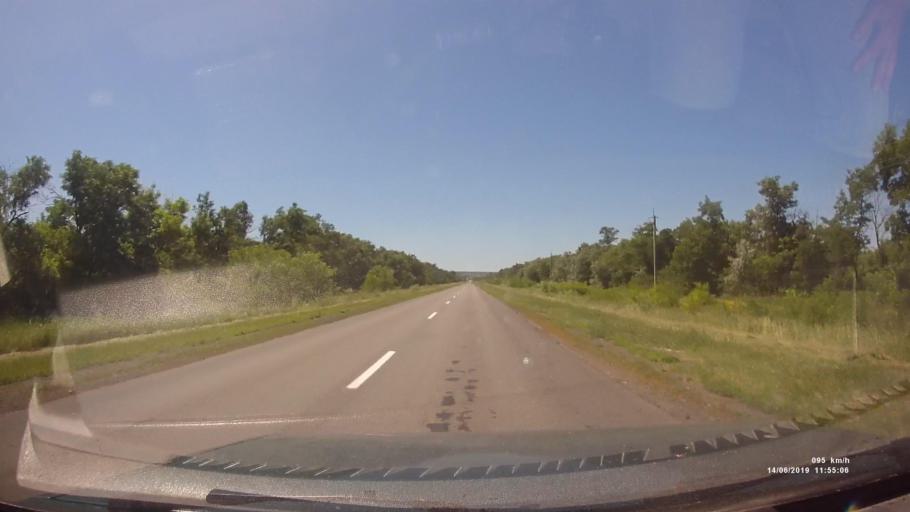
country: RU
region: Rostov
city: Kazanskaya
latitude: 49.8133
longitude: 41.1827
